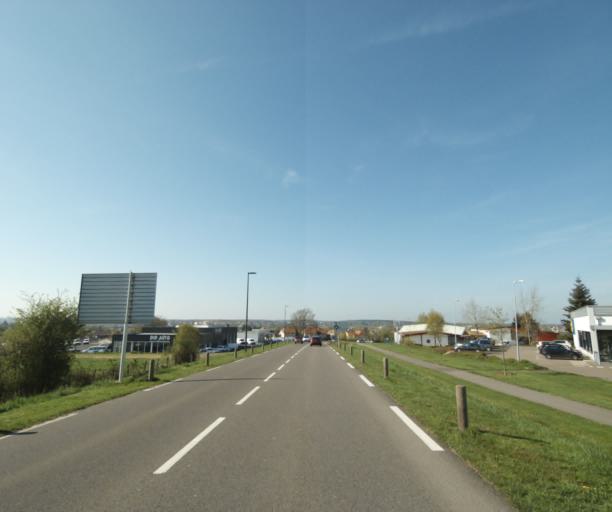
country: FR
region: Bourgogne
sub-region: Departement de Saone-et-Loire
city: Paray-le-Monial
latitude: 46.4646
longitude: 4.1170
